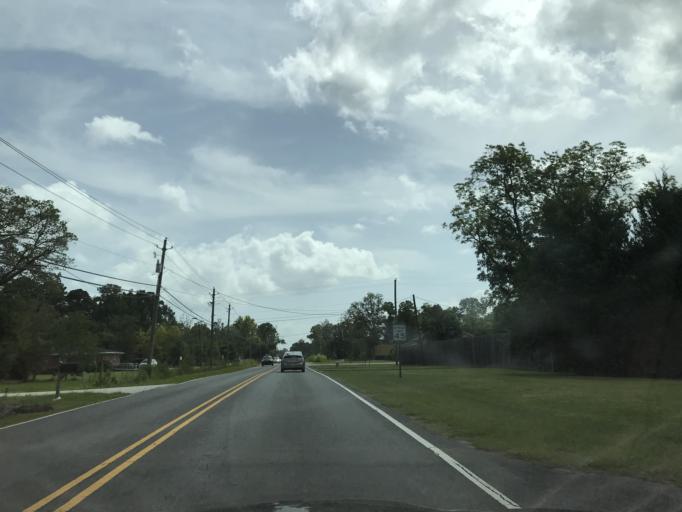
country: US
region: North Carolina
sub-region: New Hanover County
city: Wrightsboro
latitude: 34.2819
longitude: -77.9229
